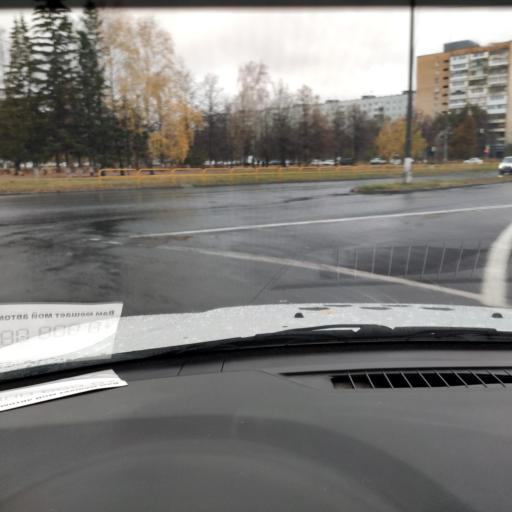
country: RU
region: Samara
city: Tol'yatti
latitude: 53.5292
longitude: 49.2783
